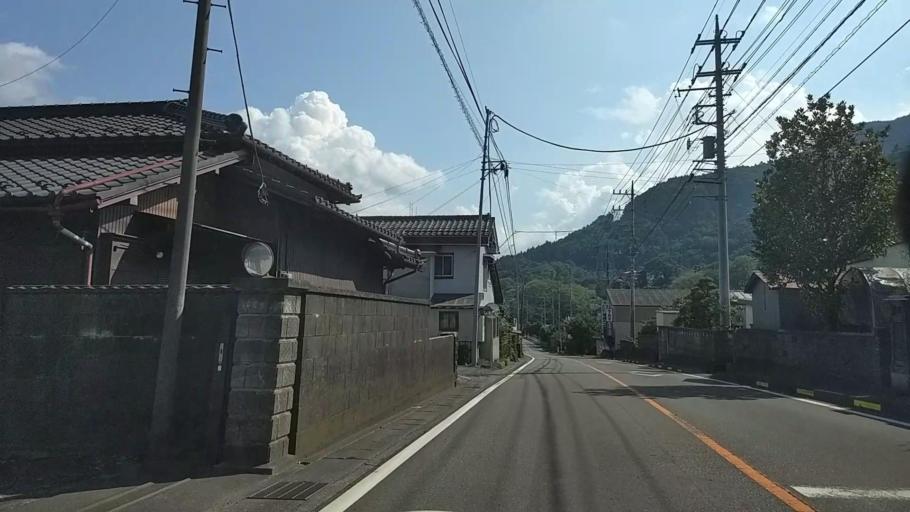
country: JP
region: Yamanashi
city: Ryuo
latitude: 35.4081
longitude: 138.4421
